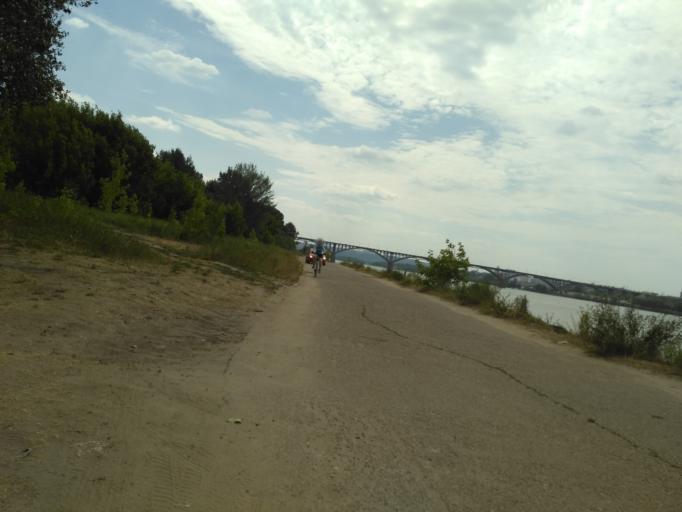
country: RU
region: Nizjnij Novgorod
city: Nizhniy Novgorod
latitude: 56.3108
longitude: 43.9683
